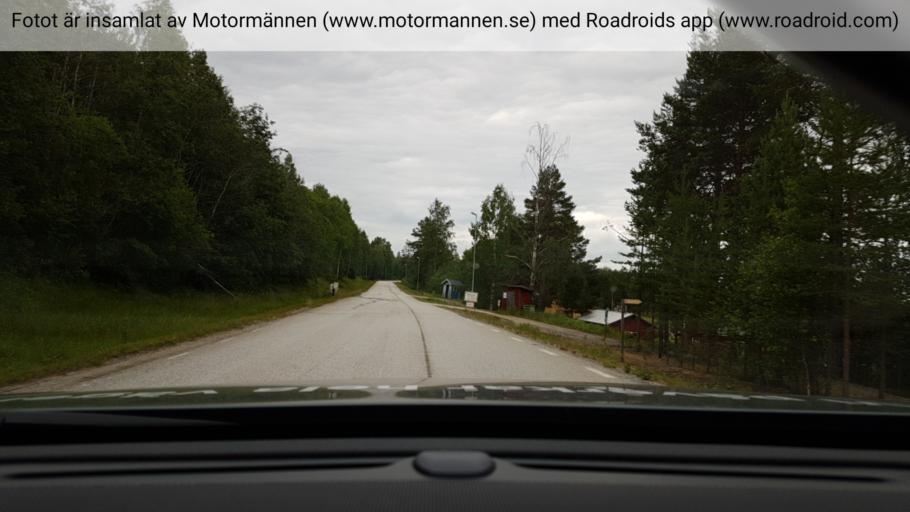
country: SE
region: Vaesterbotten
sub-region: Vannas Kommun
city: Vannasby
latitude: 64.0061
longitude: 19.9190
